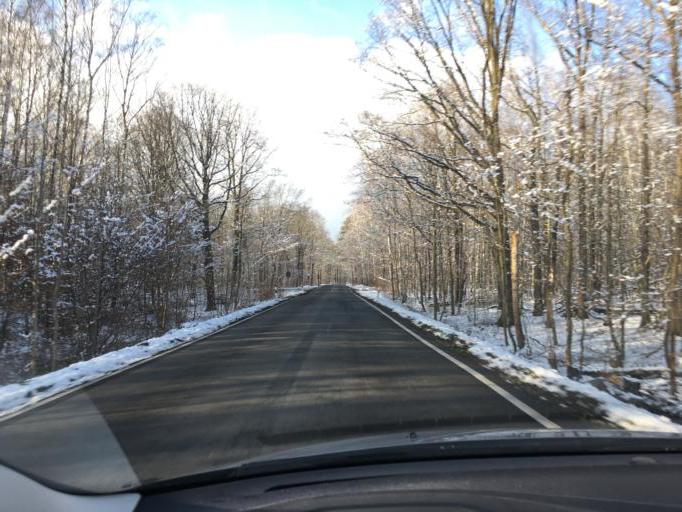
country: DE
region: Saxony
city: Grimma
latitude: 51.2681
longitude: 12.6695
